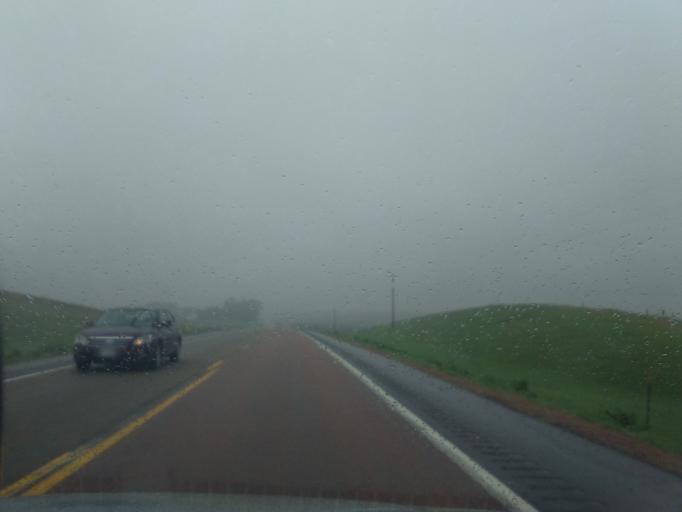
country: US
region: Nebraska
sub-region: Wayne County
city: Wayne
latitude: 42.2356
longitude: -97.0975
